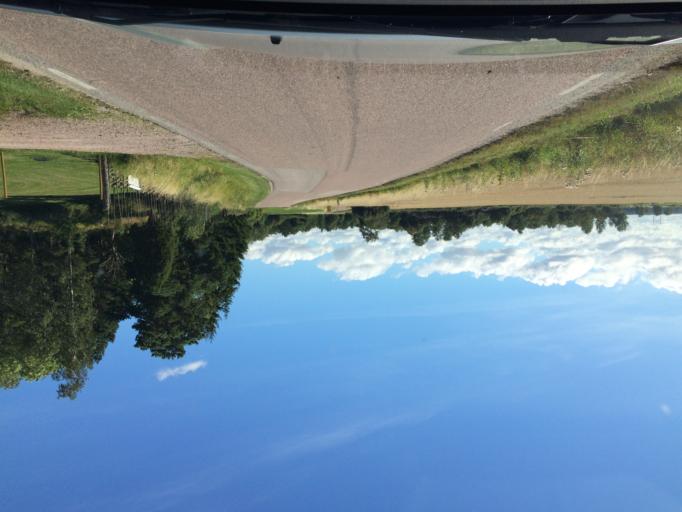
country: SE
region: Soedermanland
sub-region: Eskilstuna Kommun
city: Torshalla
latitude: 59.5313
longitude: 16.4439
